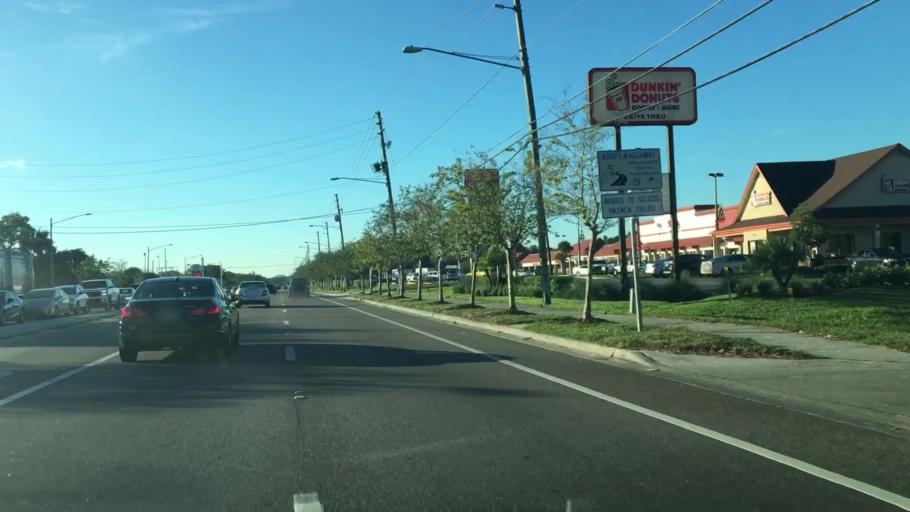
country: US
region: Florida
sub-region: Orange County
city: Azalea Park
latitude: 28.5376
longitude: -81.2858
